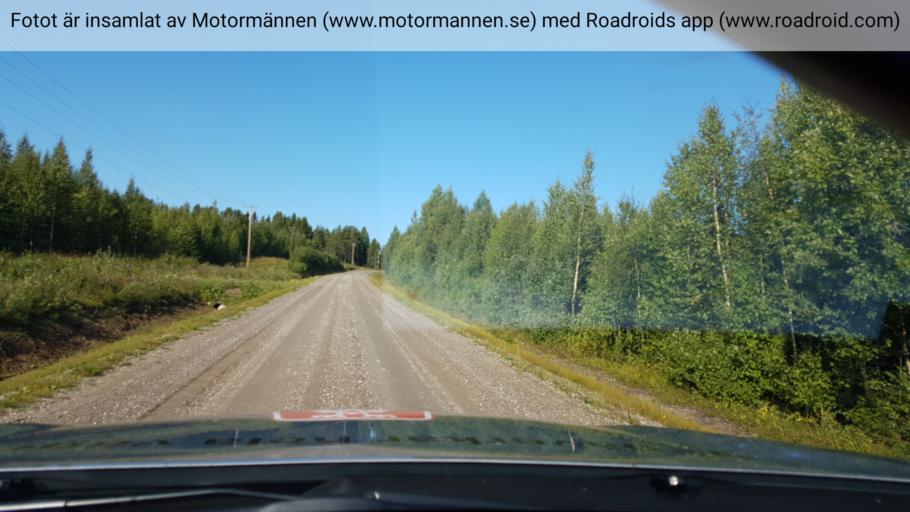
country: SE
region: Norrbotten
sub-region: Kalix Kommun
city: Kalix
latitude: 66.1353
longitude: 23.2374
